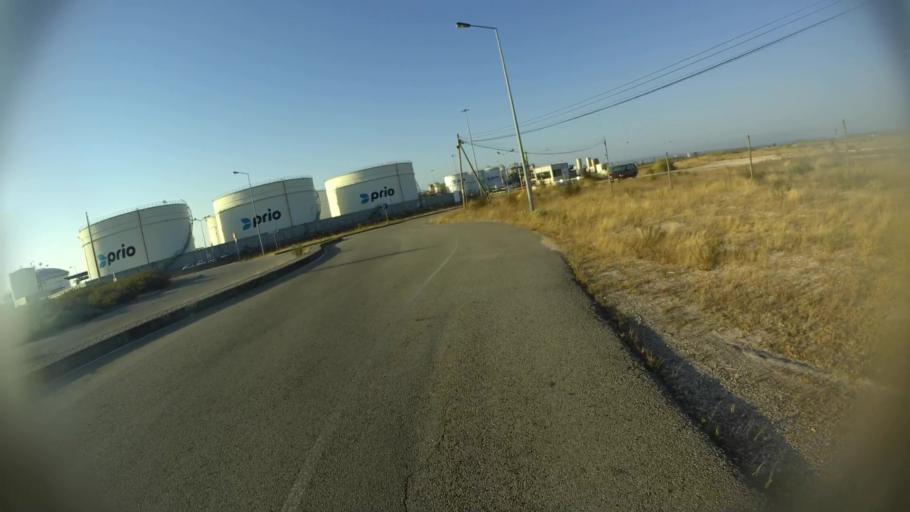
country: PT
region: Aveiro
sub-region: Ilhavo
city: Gafanha da Nazare
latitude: 40.6507
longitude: -8.7047
